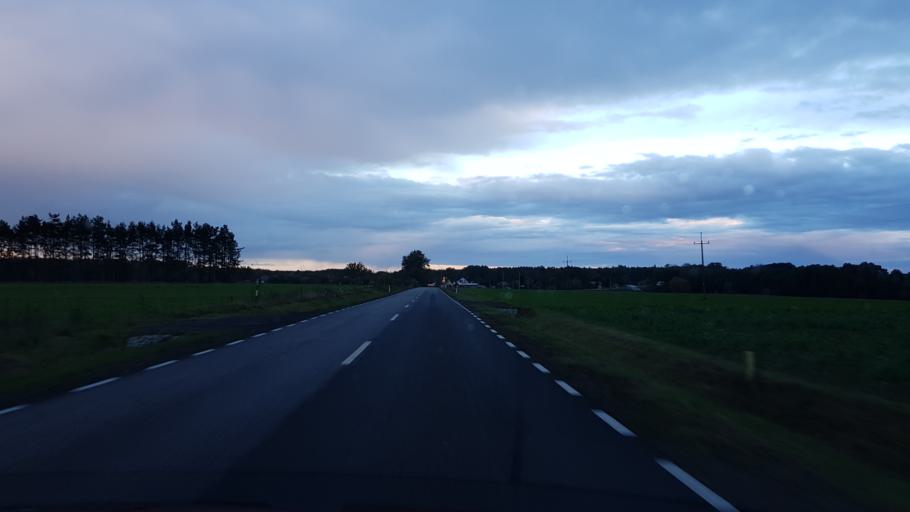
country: PL
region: Greater Poland Voivodeship
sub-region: Powiat zlotowski
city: Krajenka
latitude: 53.2732
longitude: 16.9404
